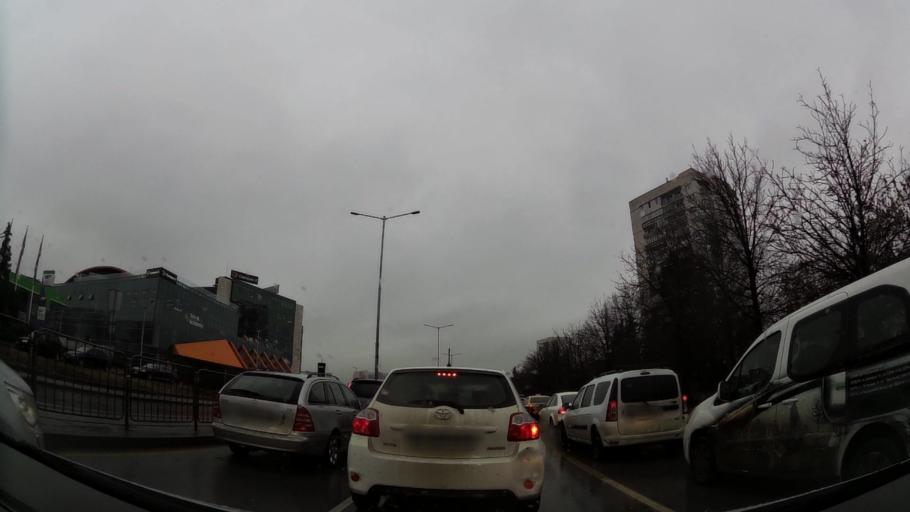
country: BG
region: Sofia-Capital
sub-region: Stolichna Obshtina
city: Sofia
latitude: 42.6515
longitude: 23.3791
